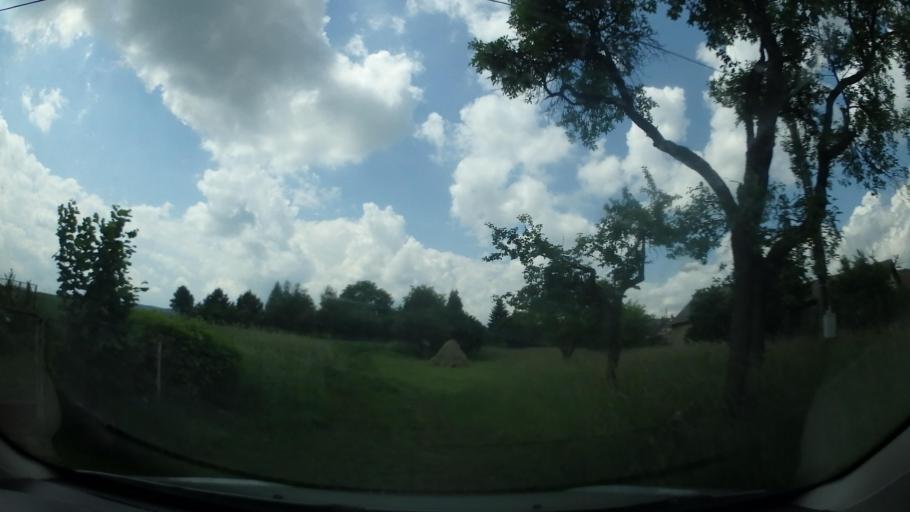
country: CZ
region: South Moravian
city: Velke Opatovice
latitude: 49.5638
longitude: 16.6733
